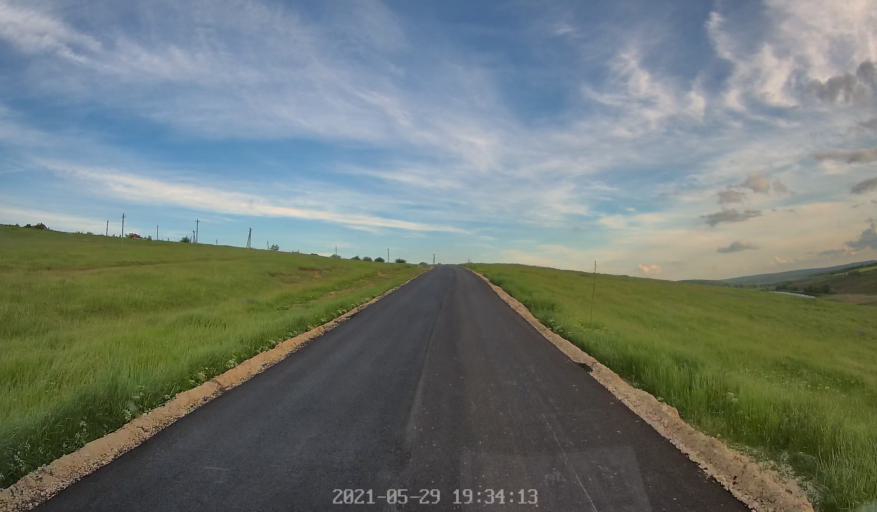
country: MD
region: Chisinau
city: Singera
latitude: 46.8278
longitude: 28.9595
